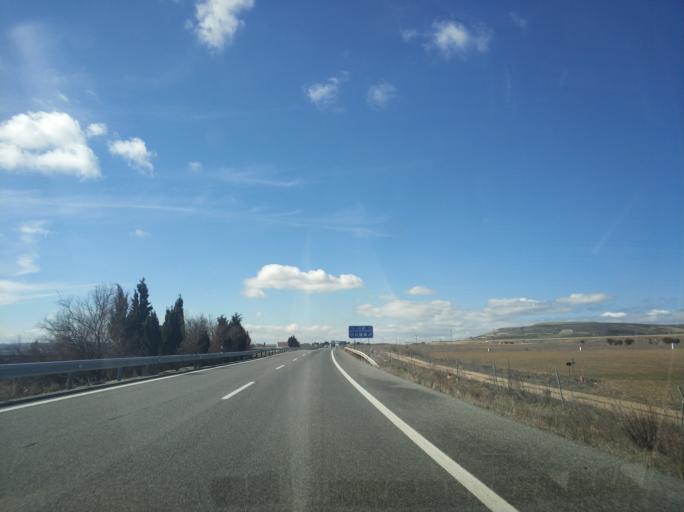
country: ES
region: Castille and Leon
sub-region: Provincia de Burgos
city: Villazopeque
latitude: 42.2117
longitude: -4.0085
